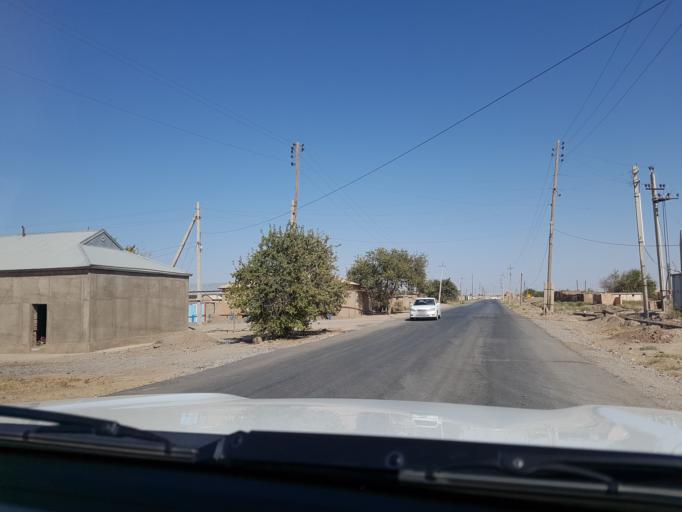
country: IR
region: Razavi Khorasan
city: Sarakhs
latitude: 36.5129
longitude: 61.2190
